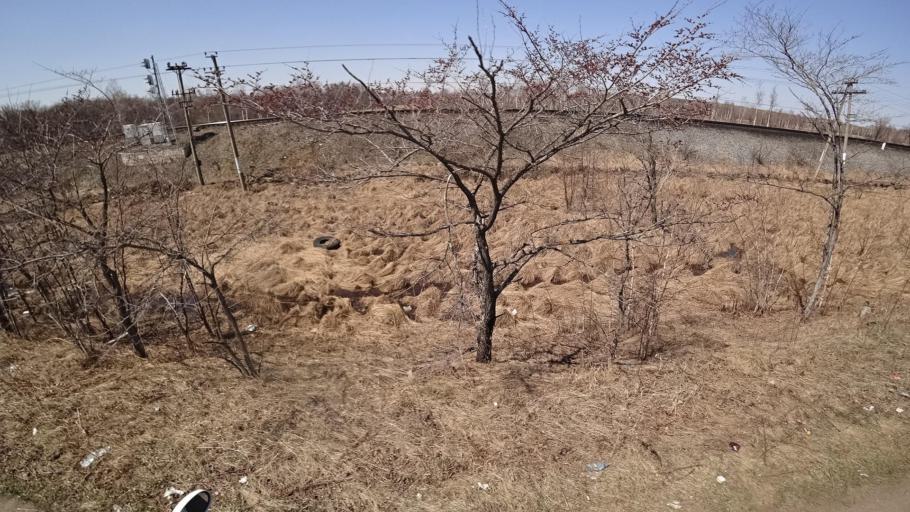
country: RU
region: Khabarovsk Krai
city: Khurba
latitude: 50.4008
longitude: 136.8654
